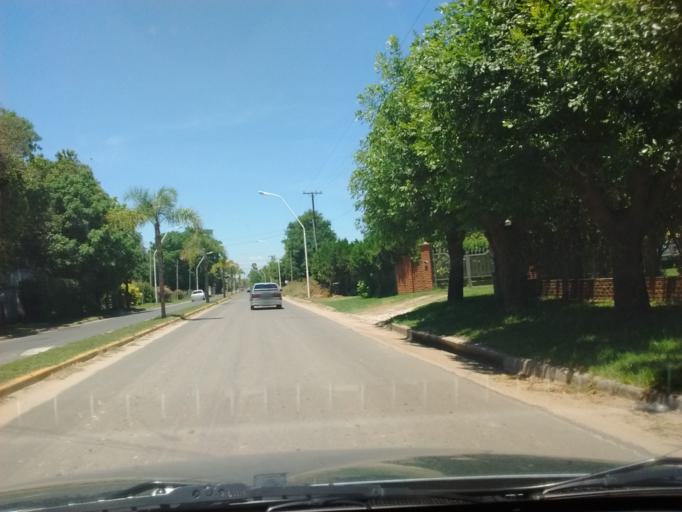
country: AR
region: Entre Rios
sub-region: Departamento de Gualeguay
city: Gualeguay
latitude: -33.1341
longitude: -59.3242
